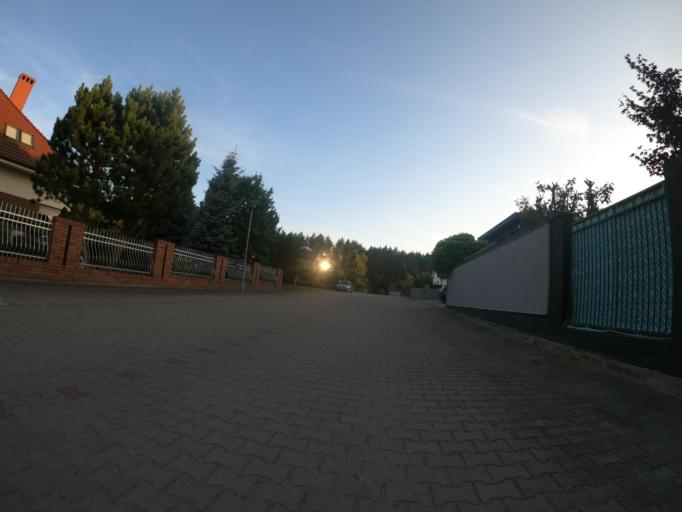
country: PL
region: West Pomeranian Voivodeship
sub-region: Powiat policki
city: Dobra
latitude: 53.4571
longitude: 14.4535
